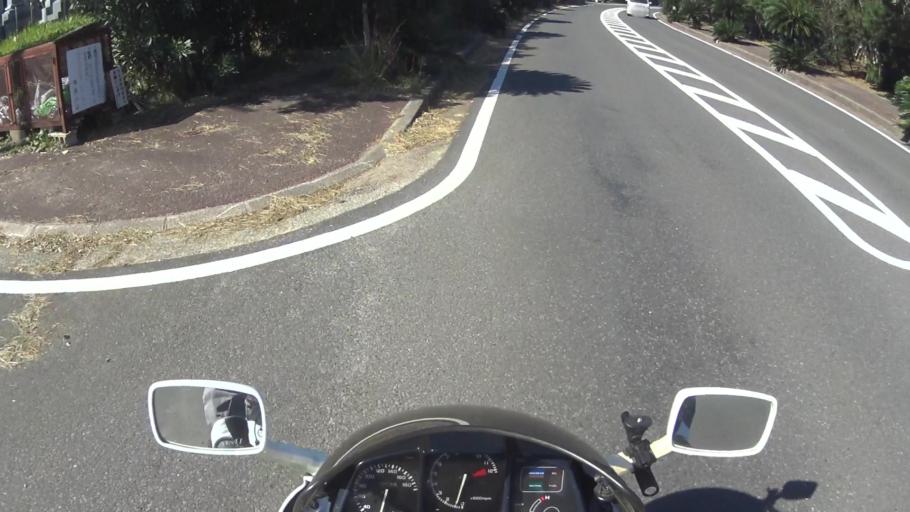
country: JP
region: Kyoto
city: Miyazu
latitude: 35.6893
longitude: 135.0207
